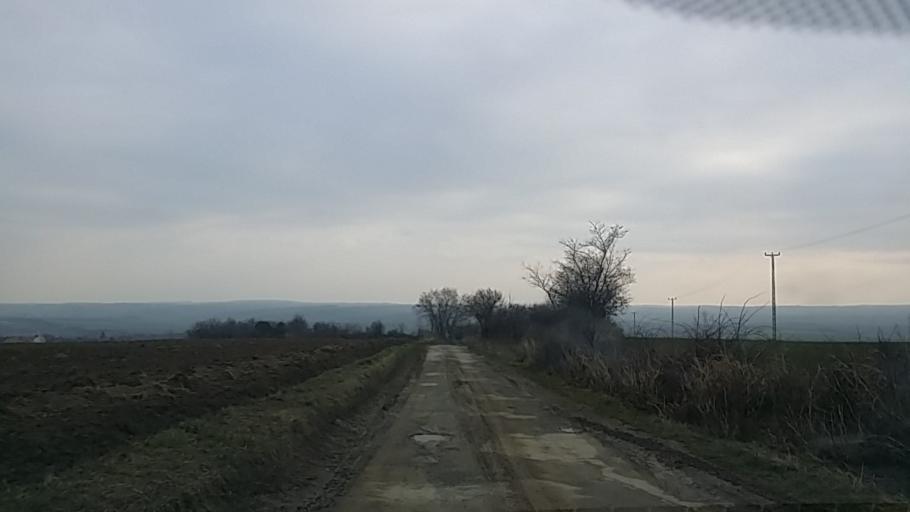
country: HU
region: Baranya
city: Pecsvarad
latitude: 46.1175
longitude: 18.5271
